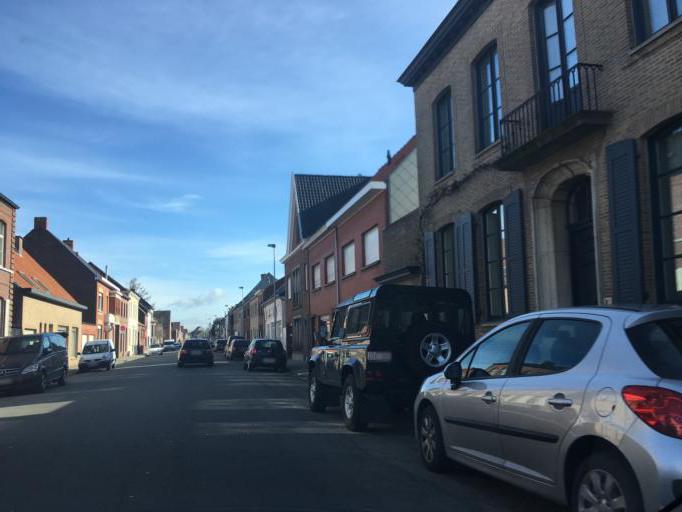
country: BE
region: Flanders
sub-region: Provincie West-Vlaanderen
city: Ledegem
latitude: 50.8564
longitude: 3.1293
